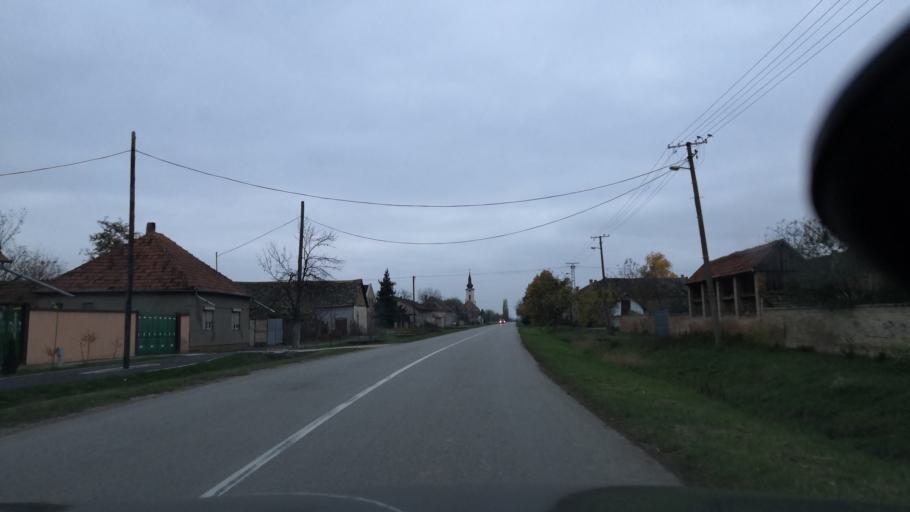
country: RS
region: Autonomna Pokrajina Vojvodina
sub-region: Severnobanatski Okrug
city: Kanjiza
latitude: 46.1304
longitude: 20.0937
